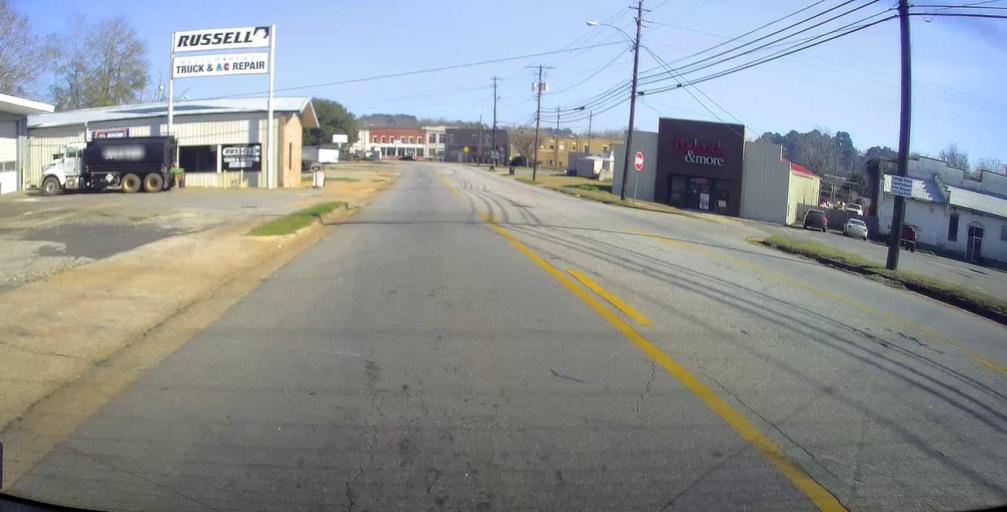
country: US
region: Georgia
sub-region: Macon County
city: Montezuma
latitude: 32.3010
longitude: -84.0321
